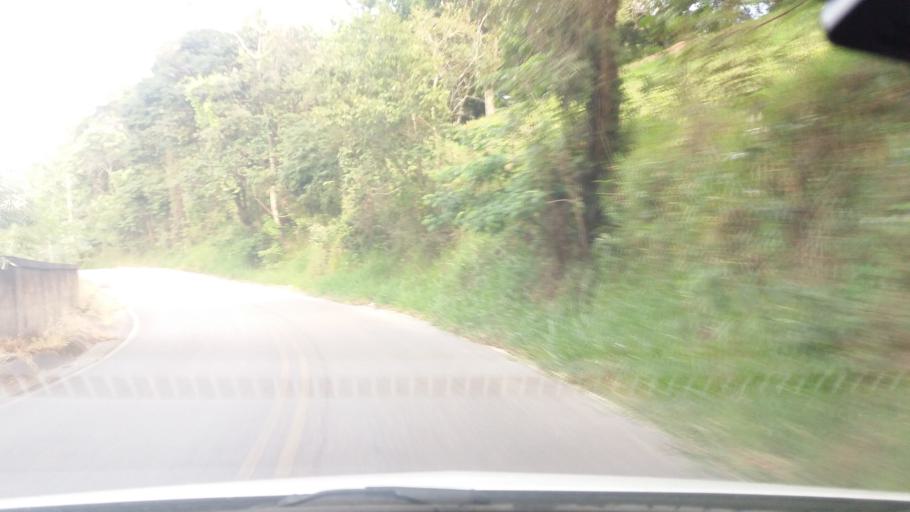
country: BR
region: Sao Paulo
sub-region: Bom Jesus Dos Perdoes
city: Bom Jesus dos Perdoes
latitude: -23.1804
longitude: -46.4868
